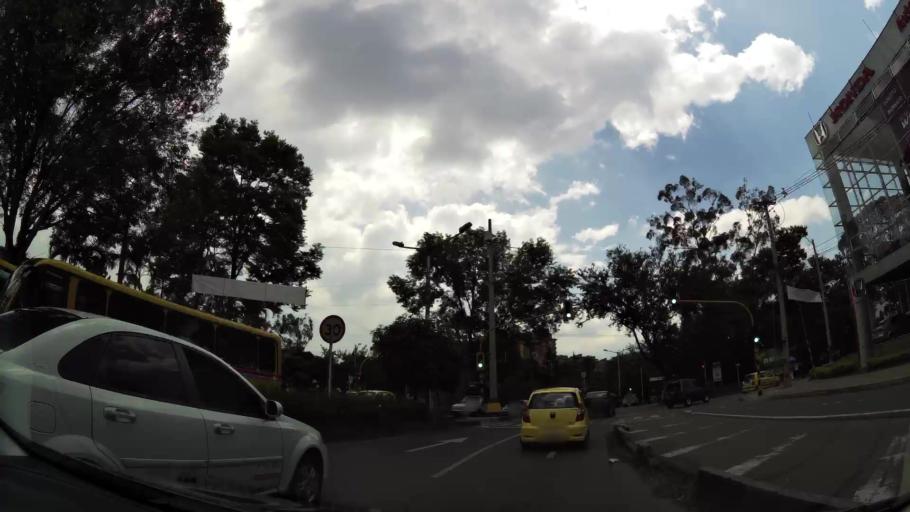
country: CO
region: Antioquia
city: Envigado
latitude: 6.1816
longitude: -75.5810
